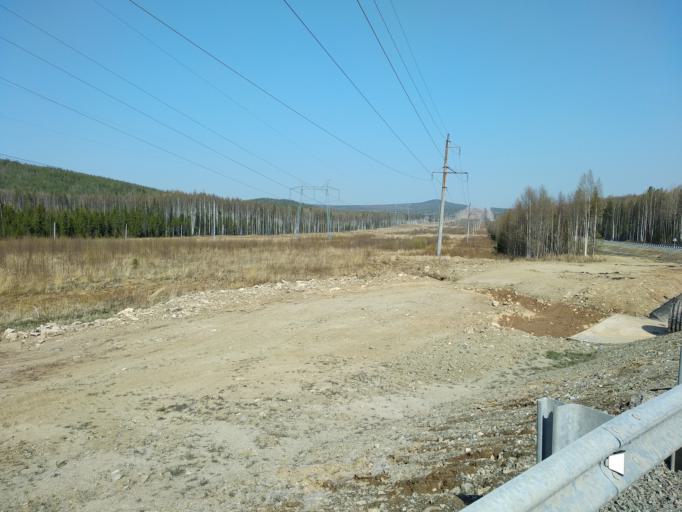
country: RU
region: Sverdlovsk
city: Karpinsk
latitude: 59.5871
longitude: 59.4586
